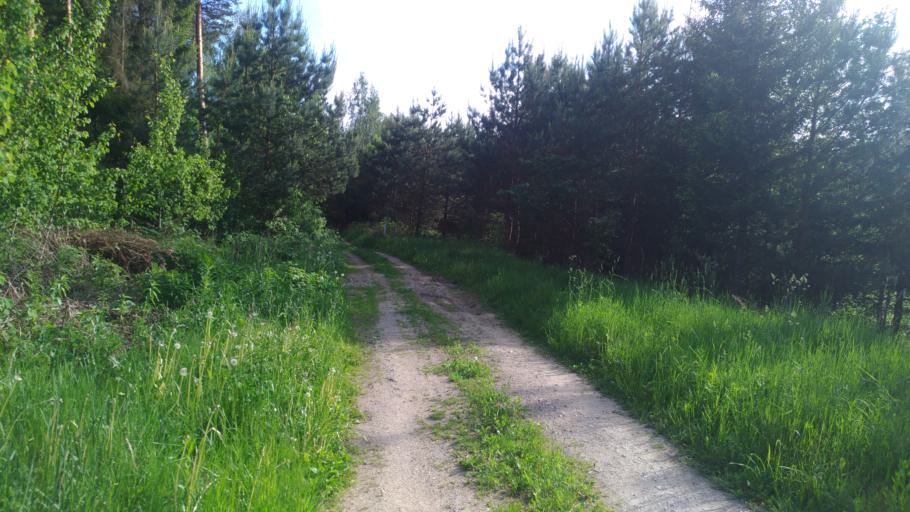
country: LT
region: Kauno apskritis
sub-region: Kauno rajonas
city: Karmelava
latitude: 54.9892
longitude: 24.1119
